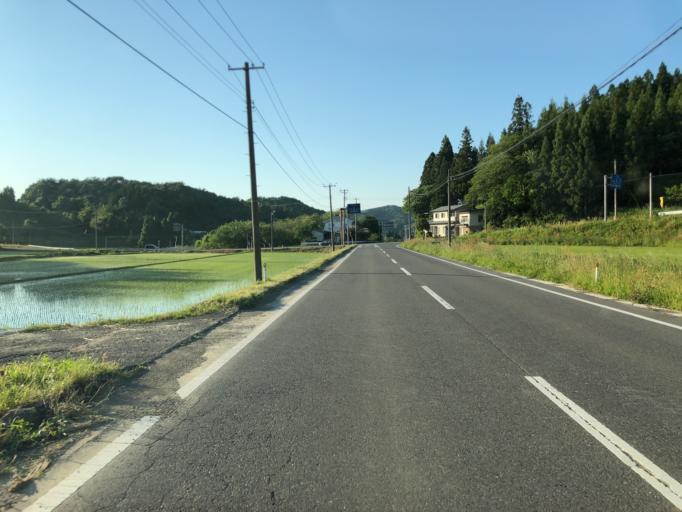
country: JP
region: Fukushima
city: Ishikawa
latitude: 37.0303
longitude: 140.4338
